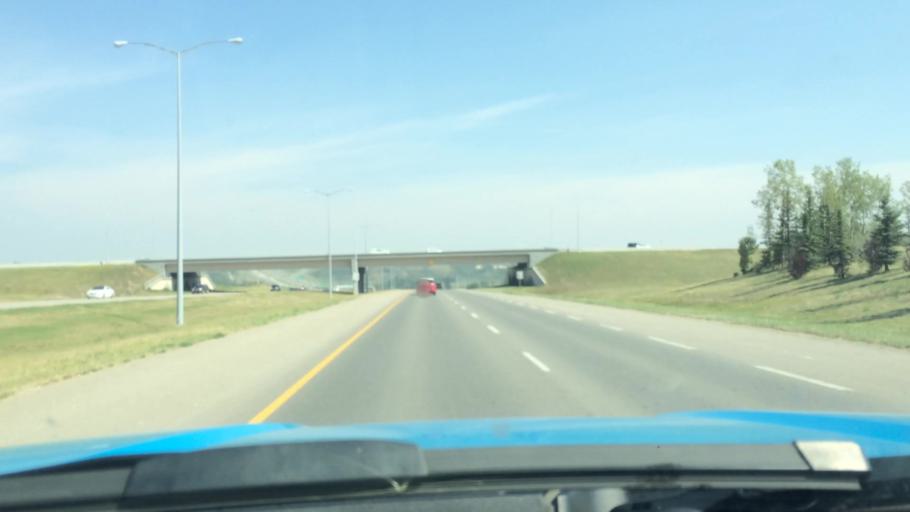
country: CA
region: Alberta
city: Calgary
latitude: 50.8926
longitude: -114.0284
